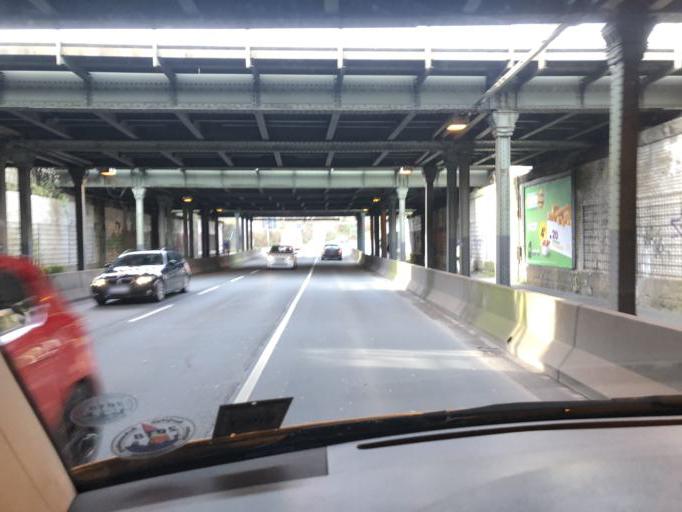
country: DE
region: North Rhine-Westphalia
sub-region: Regierungsbezirk Detmold
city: Herford
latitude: 52.1179
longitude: 8.6627
